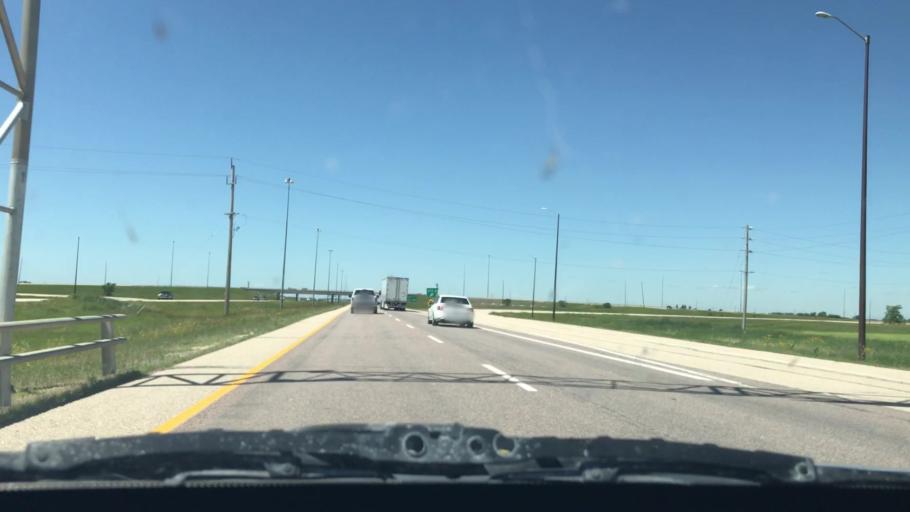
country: CA
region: Manitoba
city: Steinbach
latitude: 49.6981
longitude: -96.6383
